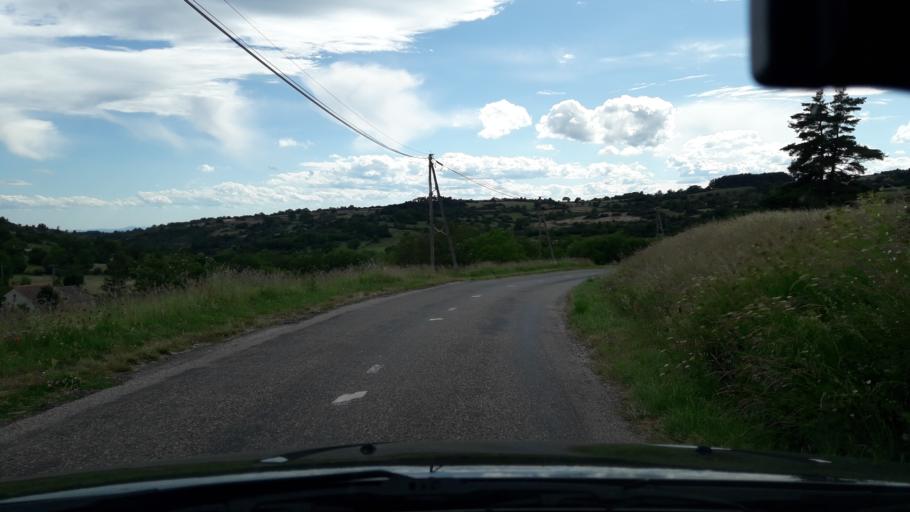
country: FR
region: Rhone-Alpes
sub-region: Departement de l'Ardeche
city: Saint-Priest
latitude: 44.6830
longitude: 4.5457
